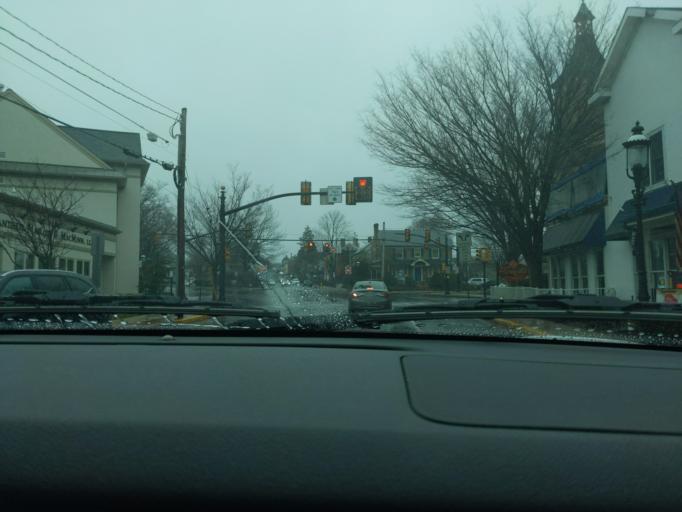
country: US
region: Pennsylvania
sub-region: Bucks County
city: Doylestown
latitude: 40.3085
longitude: -75.1337
